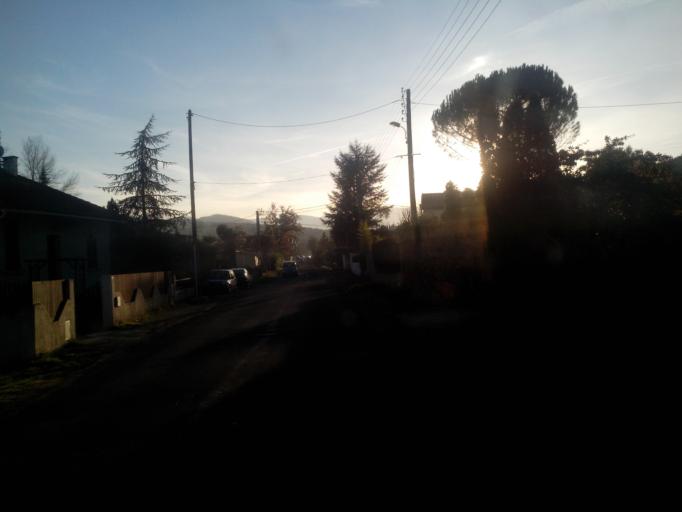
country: FR
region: Languedoc-Roussillon
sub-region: Departement de l'Aude
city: Esperaza
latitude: 42.9410
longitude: 2.2350
